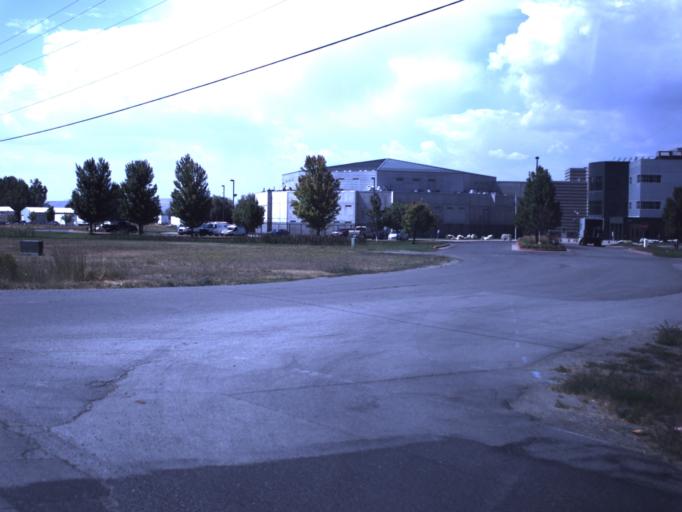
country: US
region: Utah
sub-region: Cache County
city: Logan
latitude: 41.7357
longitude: -111.8646
